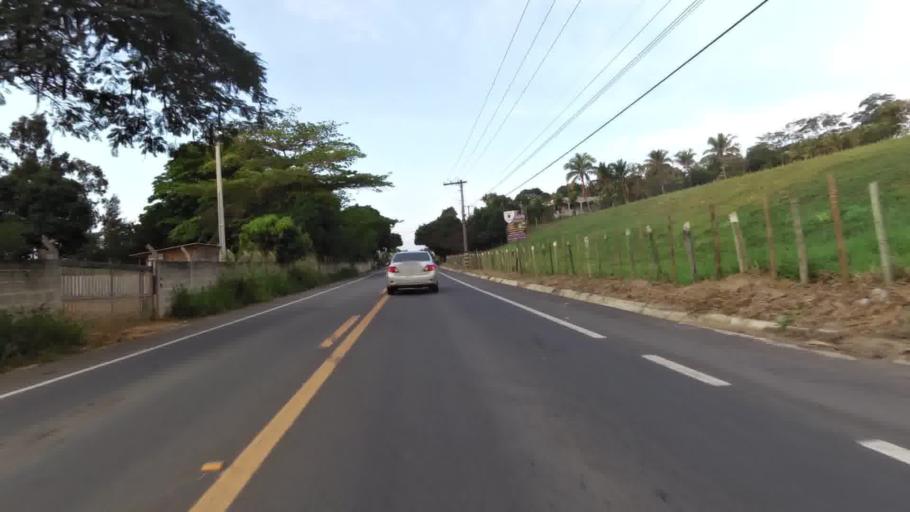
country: BR
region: Espirito Santo
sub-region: Piuma
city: Piuma
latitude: -20.8175
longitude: -40.6906
